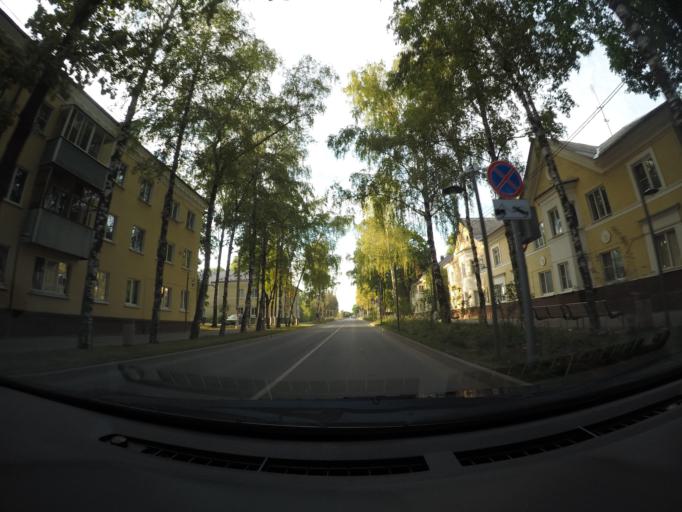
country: RU
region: Moskovskaya
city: Rechitsy
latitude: 55.5868
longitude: 38.5040
